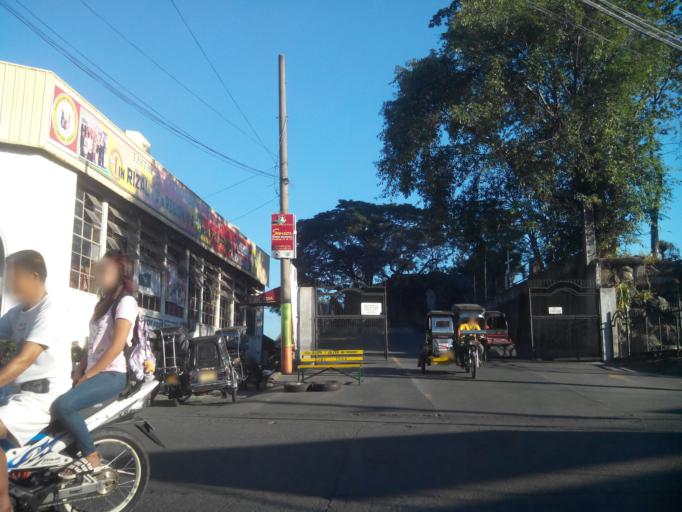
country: PH
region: Calabarzon
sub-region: Province of Rizal
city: Taytay
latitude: 14.5702
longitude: 121.1320
